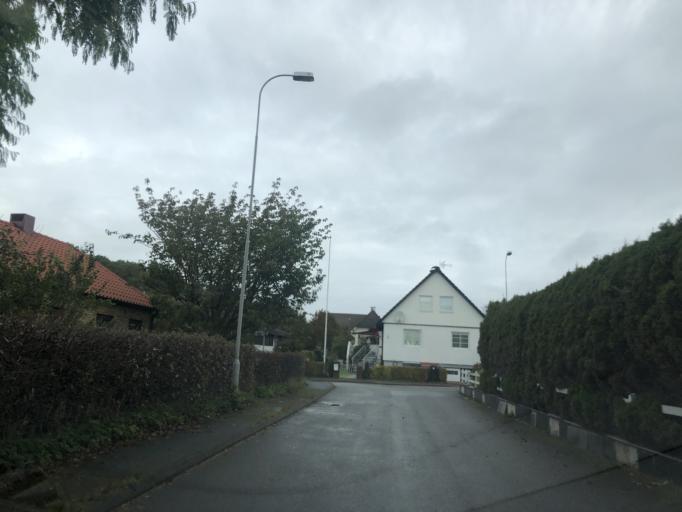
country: SE
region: Vaestra Goetaland
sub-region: Goteborg
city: Majorna
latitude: 57.6688
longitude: 11.9036
